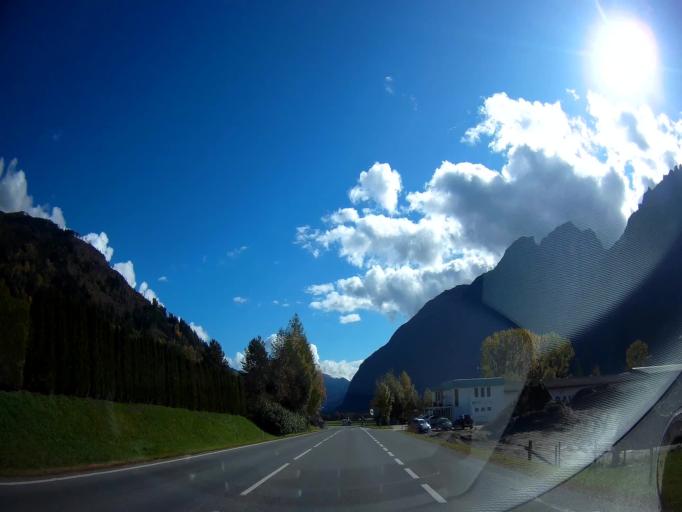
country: AT
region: Tyrol
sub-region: Politischer Bezirk Lienz
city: Dolsach
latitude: 46.8140
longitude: 12.8442
